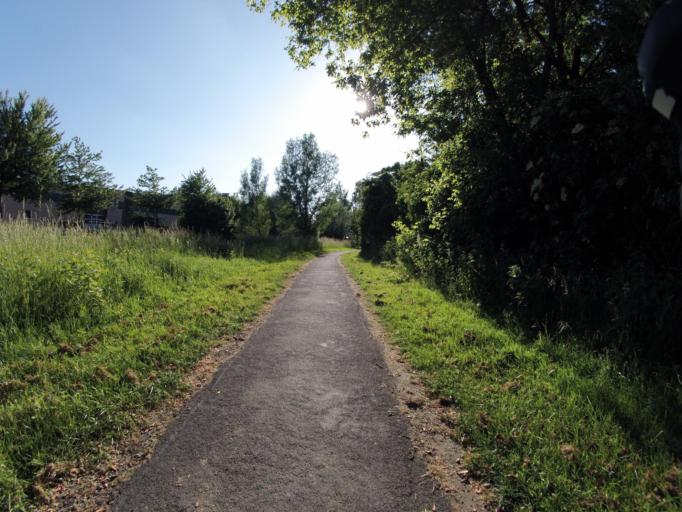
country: DE
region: Lower Saxony
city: Schuttorf
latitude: 52.3198
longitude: 7.2293
